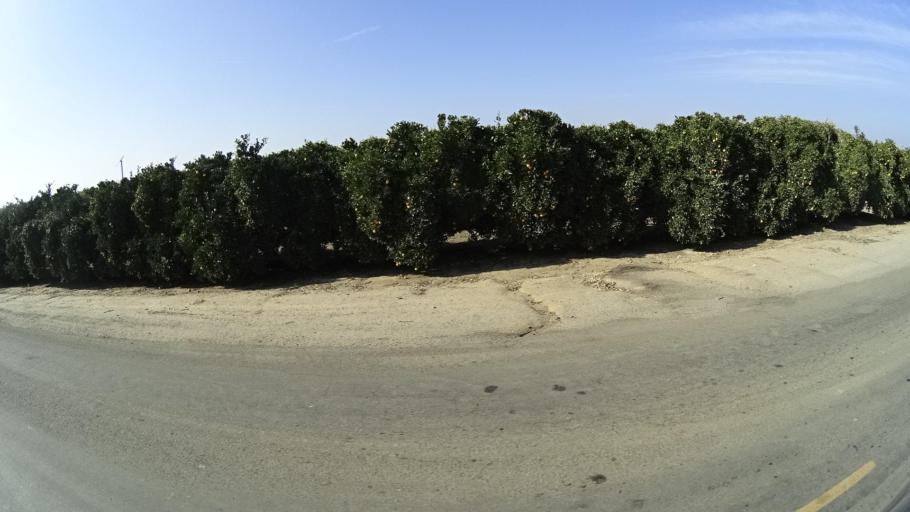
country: US
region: California
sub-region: Kern County
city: McFarland
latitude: 35.6724
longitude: -119.1693
